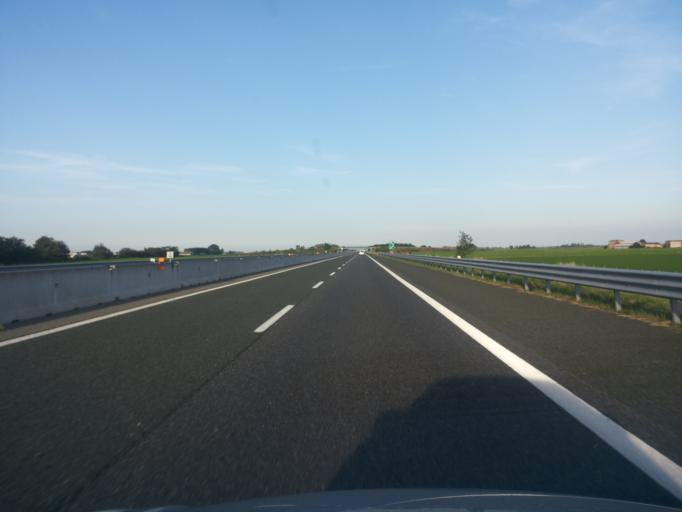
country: IT
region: Piedmont
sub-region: Provincia di Vercelli
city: Sali Vercellese
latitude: 45.3042
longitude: 8.3125
